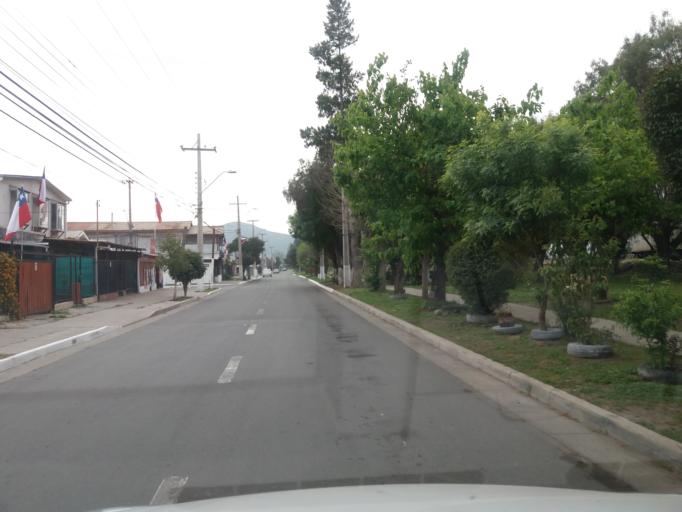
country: CL
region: Valparaiso
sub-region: Provincia de Quillota
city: Hacienda La Calera
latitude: -32.7835
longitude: -71.1746
